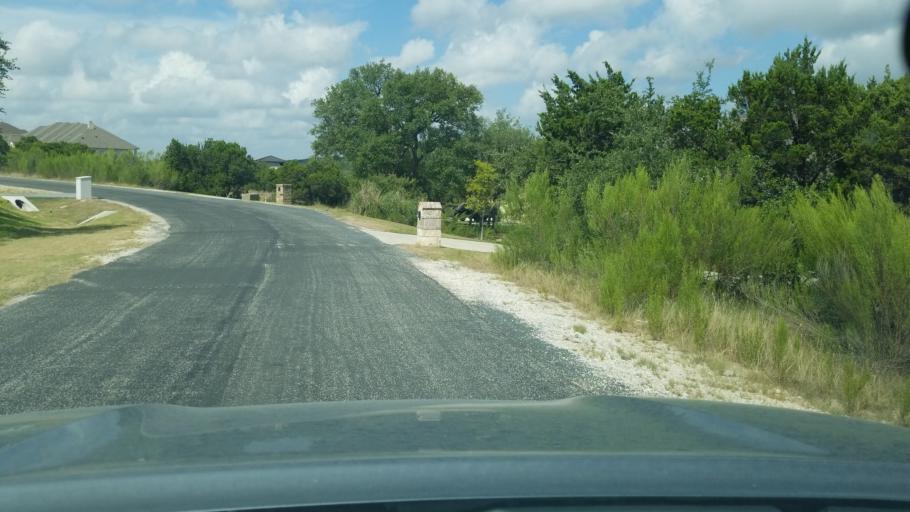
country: US
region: Texas
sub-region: Bexar County
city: Timberwood Park
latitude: 29.6866
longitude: -98.5184
